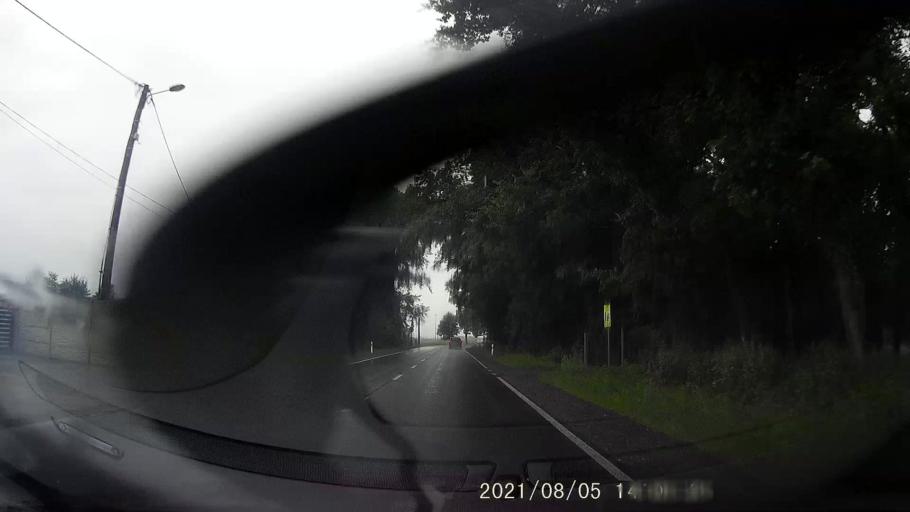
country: PL
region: Opole Voivodeship
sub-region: Powiat krapkowicki
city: Strzeleczki
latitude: 50.4476
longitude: 17.8943
